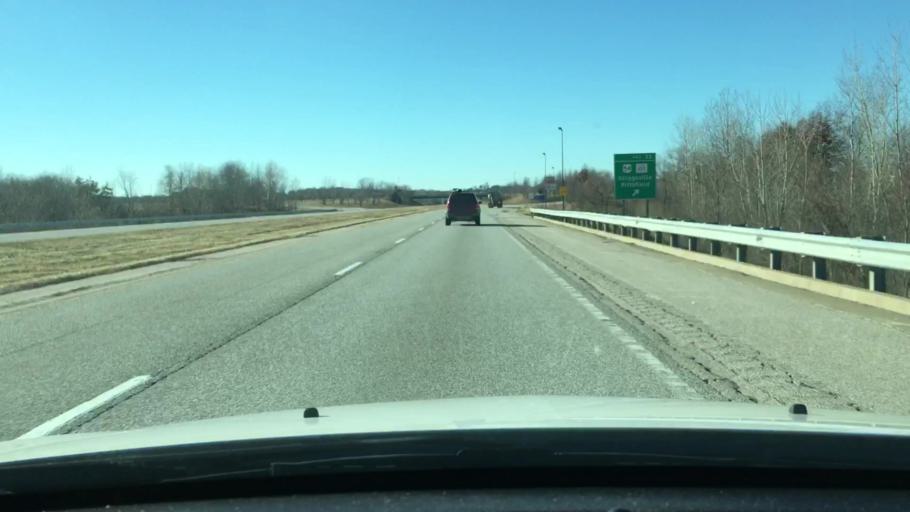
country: US
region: Illinois
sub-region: Pike County
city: Griggsville
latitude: 39.6742
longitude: -90.7612
